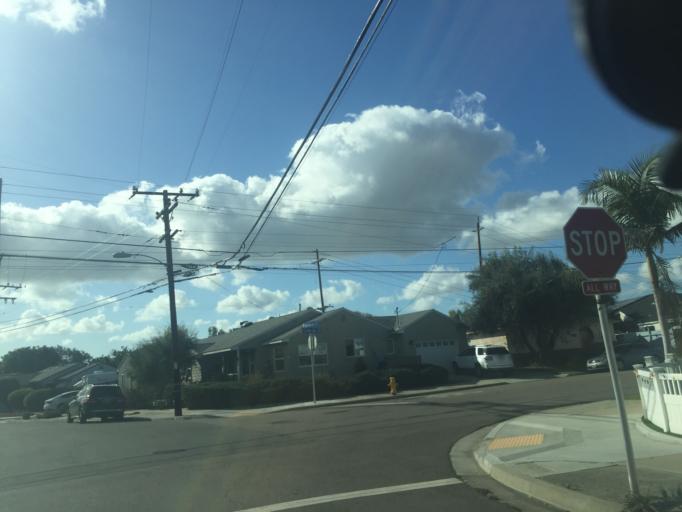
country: US
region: California
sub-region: San Diego County
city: La Mesa
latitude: 32.7882
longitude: -117.0897
